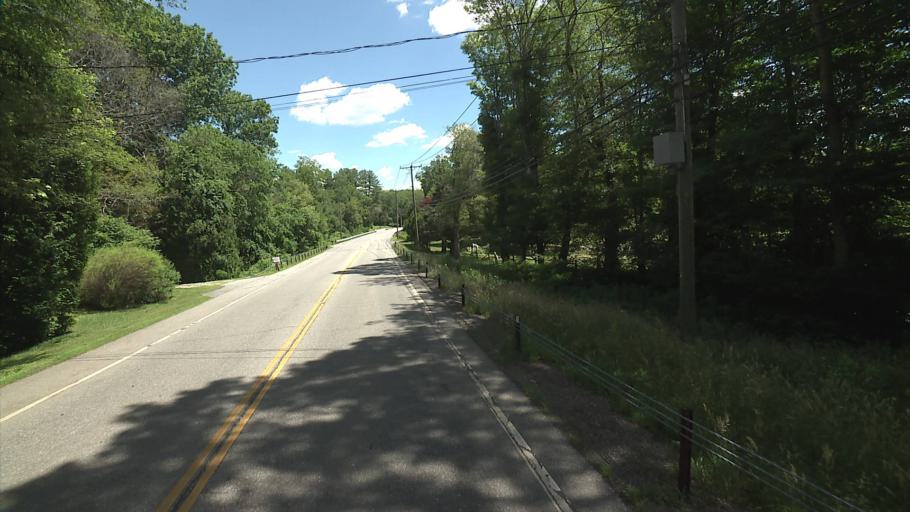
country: US
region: Connecticut
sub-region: New London County
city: Pawcatuck
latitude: 41.4292
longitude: -71.8533
